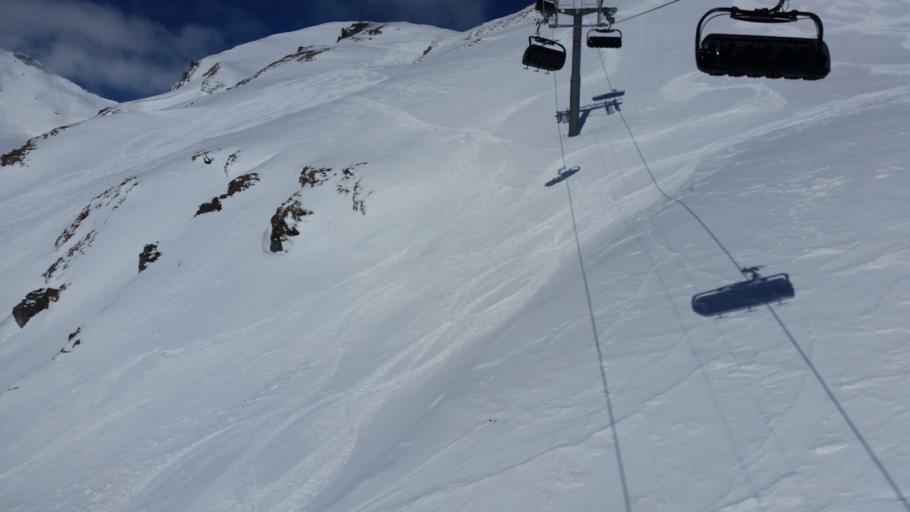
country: CH
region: Grisons
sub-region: Surselva District
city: Ilanz
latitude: 46.8546
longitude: 9.1646
